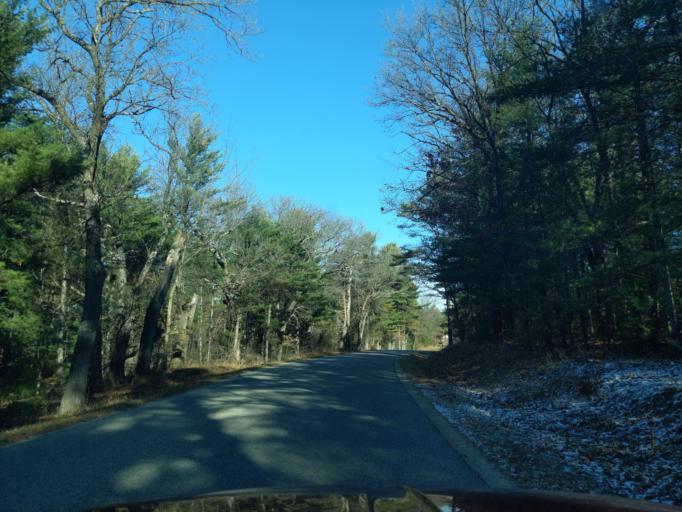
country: US
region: Wisconsin
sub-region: Waushara County
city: Silver Lake
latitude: 44.0855
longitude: -89.1939
